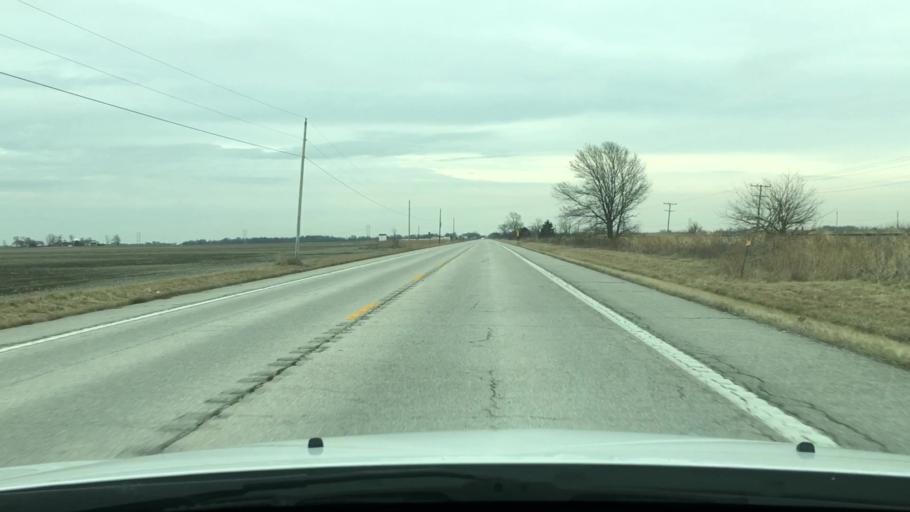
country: US
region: Missouri
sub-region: Audrain County
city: Vandalia
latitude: 39.2844
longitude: -91.5473
